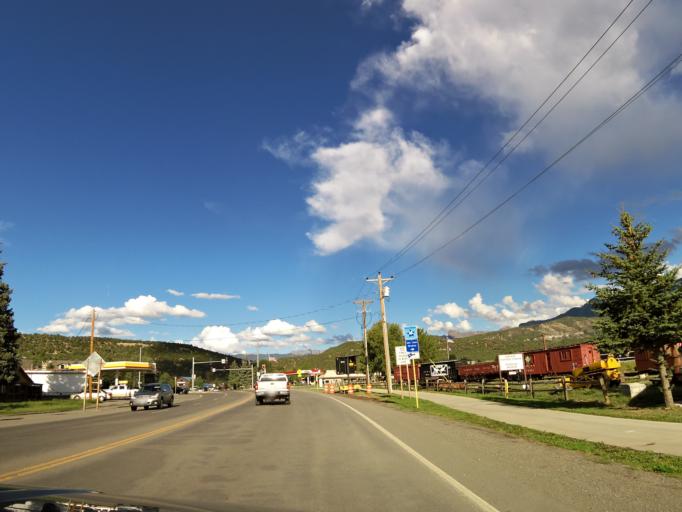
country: US
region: Colorado
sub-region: Ouray County
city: Ouray
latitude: 38.1514
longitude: -107.7500
